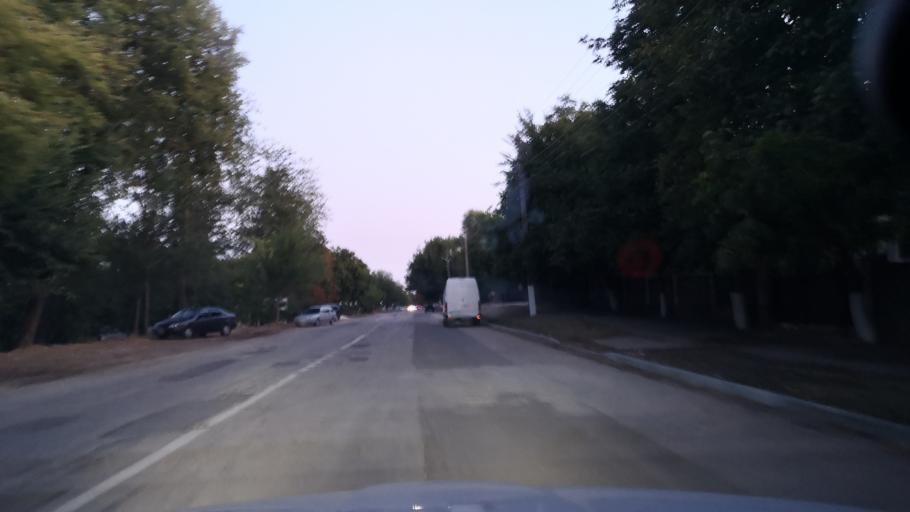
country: MD
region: Orhei
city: Orhei
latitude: 47.3921
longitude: 28.8225
